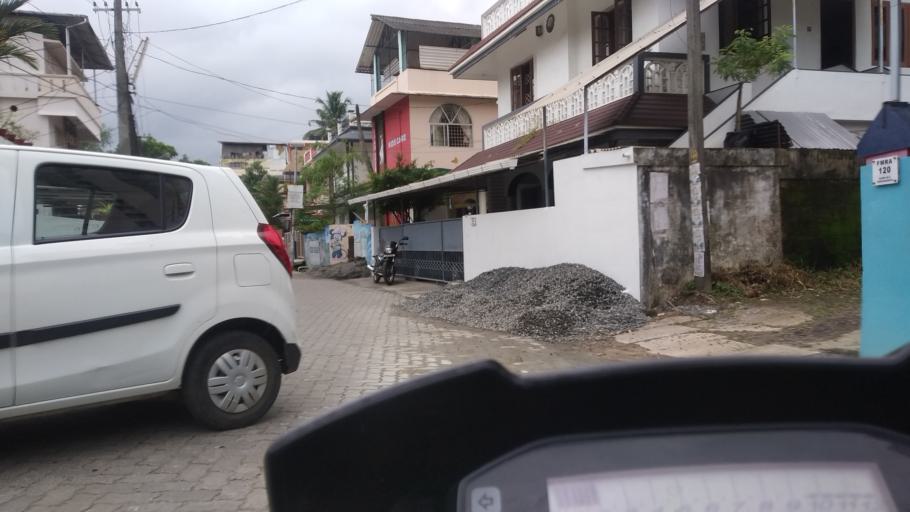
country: IN
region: Kerala
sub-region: Ernakulam
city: Cochin
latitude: 9.9827
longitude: 76.2950
